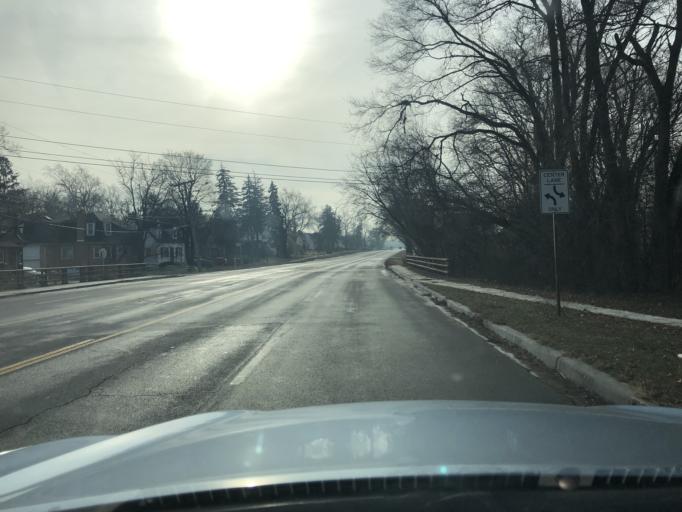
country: US
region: Illinois
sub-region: Cook County
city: Mount Prospect
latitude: 42.0492
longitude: -87.9123
